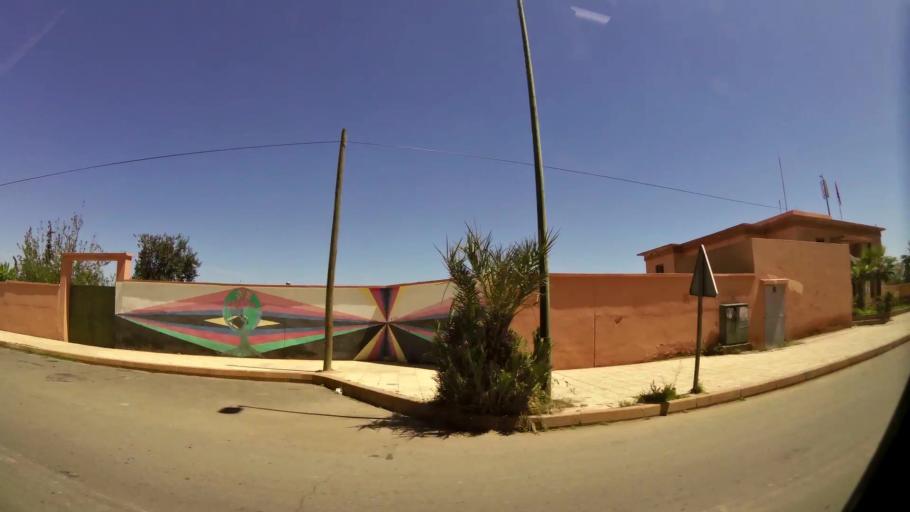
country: MA
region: Marrakech-Tensift-Al Haouz
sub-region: Marrakech
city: Marrakesh
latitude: 31.6562
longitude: -7.9859
